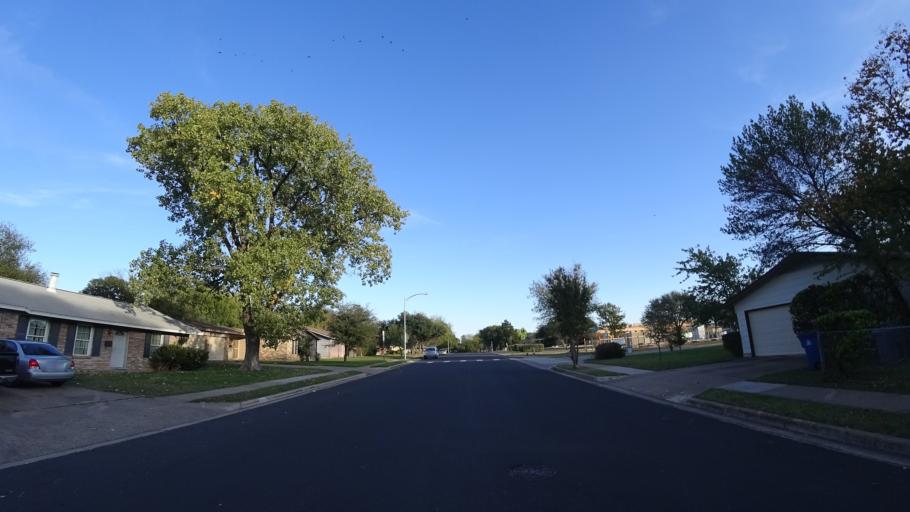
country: US
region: Texas
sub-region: Williamson County
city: Jollyville
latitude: 30.3703
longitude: -97.7347
